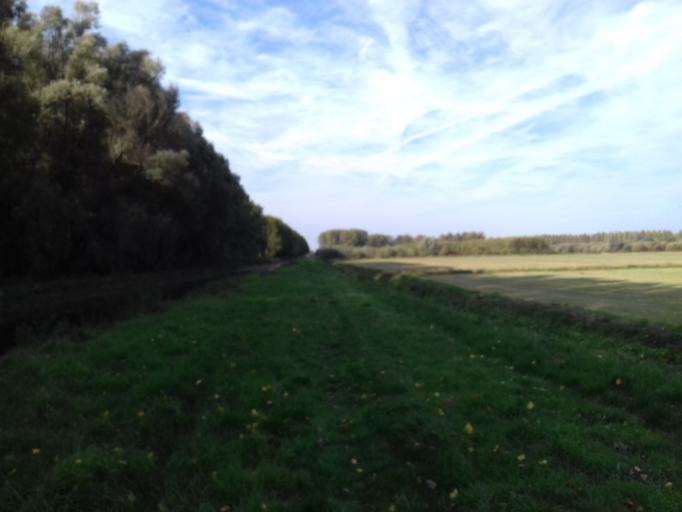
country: NL
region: Gelderland
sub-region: Gemeente Culemborg
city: Culemborg
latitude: 51.9157
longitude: 5.2393
